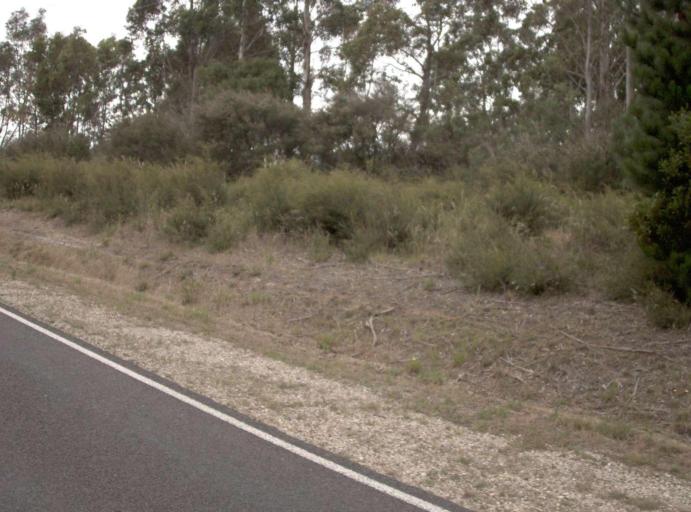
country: AU
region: Victoria
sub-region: Wellington
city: Sale
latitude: -38.1811
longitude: 147.1426
